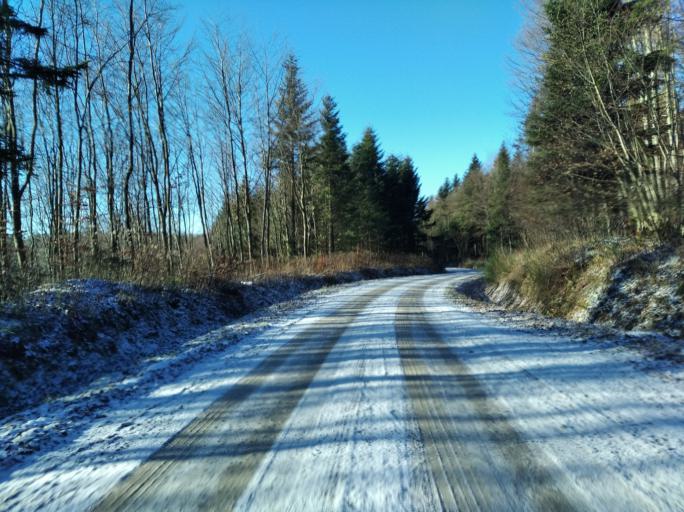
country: PL
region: Subcarpathian Voivodeship
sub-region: Powiat strzyzowski
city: Czudec
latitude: 49.9725
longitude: 21.7959
